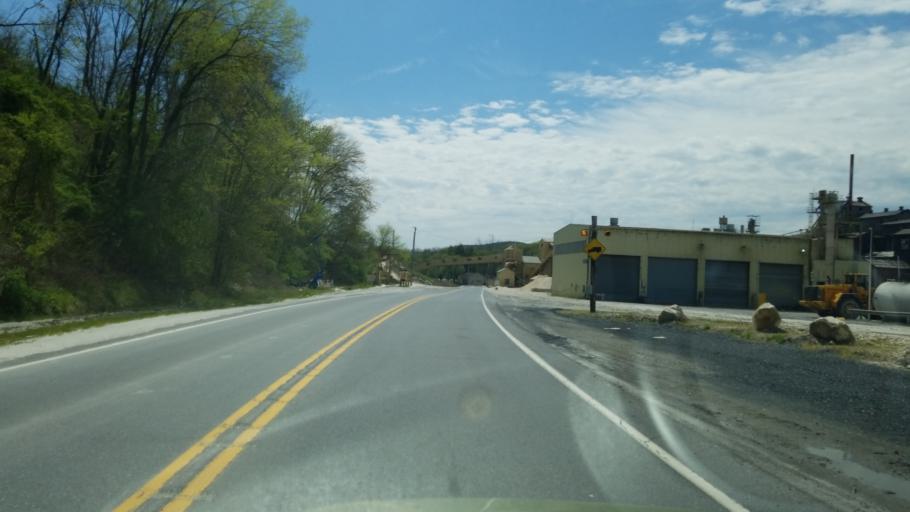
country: US
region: Pennsylvania
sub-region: Huntingdon County
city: Mount Union
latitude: 40.4093
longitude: -77.9345
